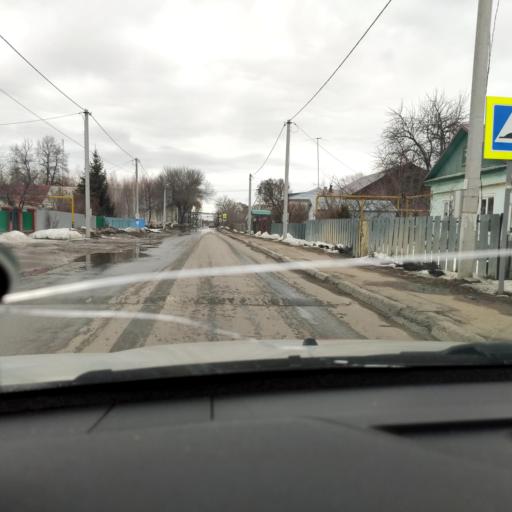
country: RU
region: Samara
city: Kurumoch
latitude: 53.4864
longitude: 50.0344
